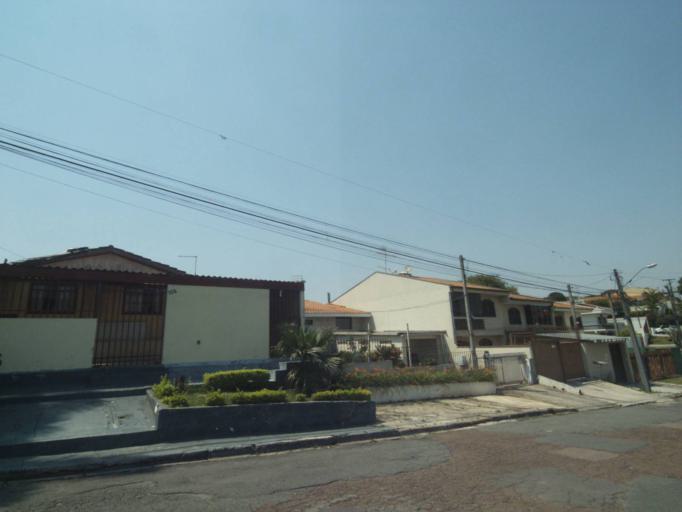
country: BR
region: Parana
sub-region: Sao Jose Dos Pinhais
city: Sao Jose dos Pinhais
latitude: -25.5055
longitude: -49.2660
